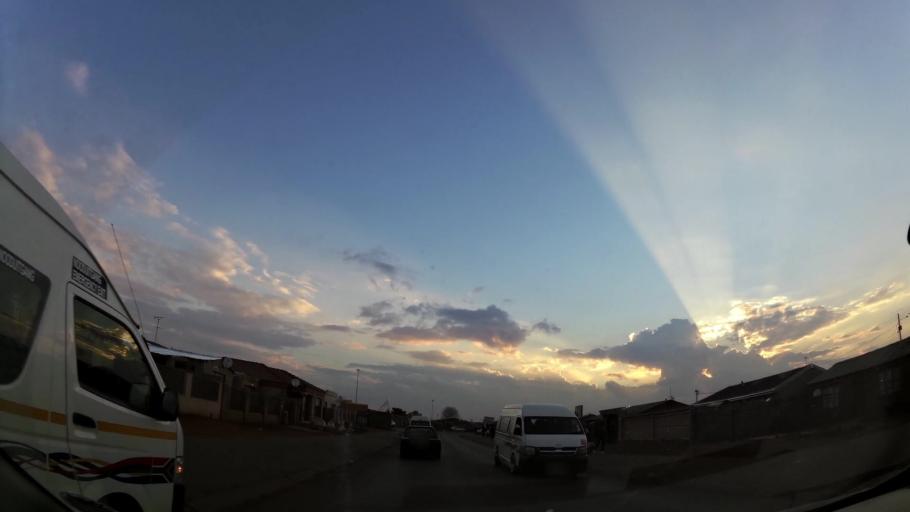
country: ZA
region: Gauteng
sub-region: City of Johannesburg Metropolitan Municipality
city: Orange Farm
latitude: -26.5504
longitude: 27.8655
